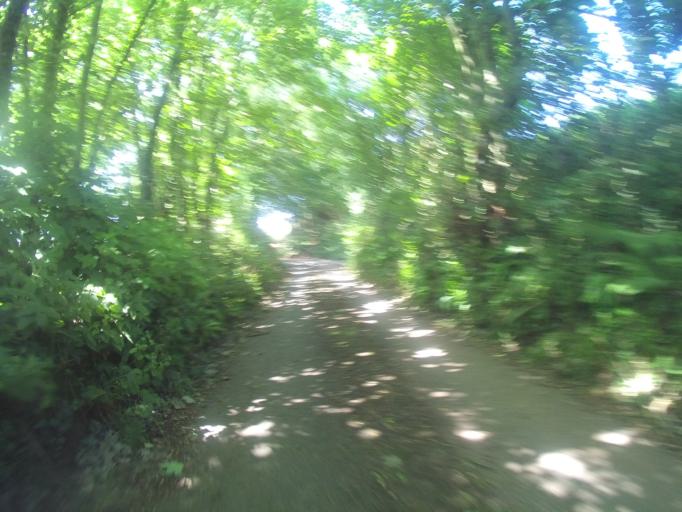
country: GB
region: England
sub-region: Devon
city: Dartmouth
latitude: 50.3626
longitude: -3.6203
